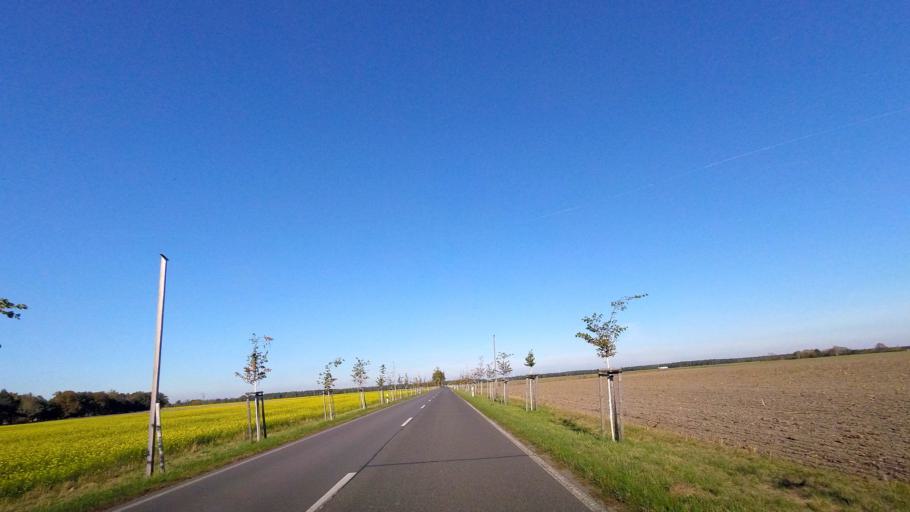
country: DE
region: Saxony-Anhalt
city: Muhlanger
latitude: 51.8411
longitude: 12.7623
